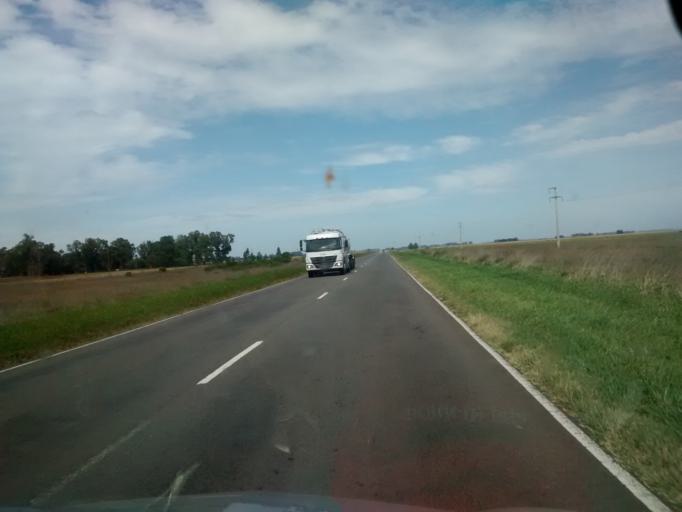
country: AR
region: Buenos Aires
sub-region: Partido de Ayacucho
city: Ayacucho
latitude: -37.0553
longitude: -58.5427
